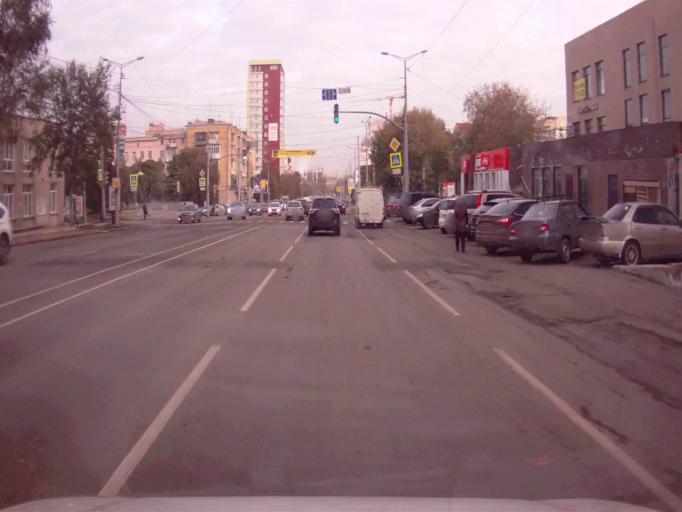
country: RU
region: Chelyabinsk
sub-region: Gorod Chelyabinsk
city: Chelyabinsk
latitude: 55.1700
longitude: 61.4114
